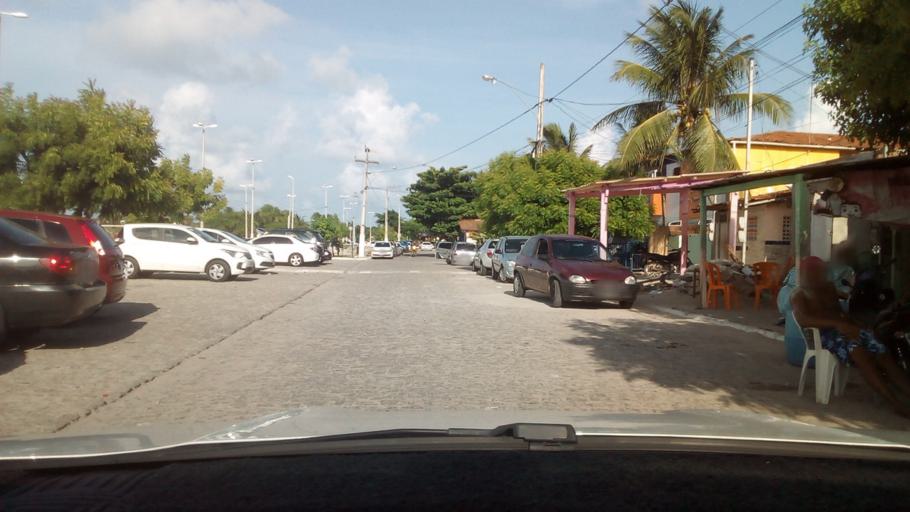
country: BR
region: Paraiba
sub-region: Cabedelo
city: Cabedelo
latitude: -6.9659
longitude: -34.8360
